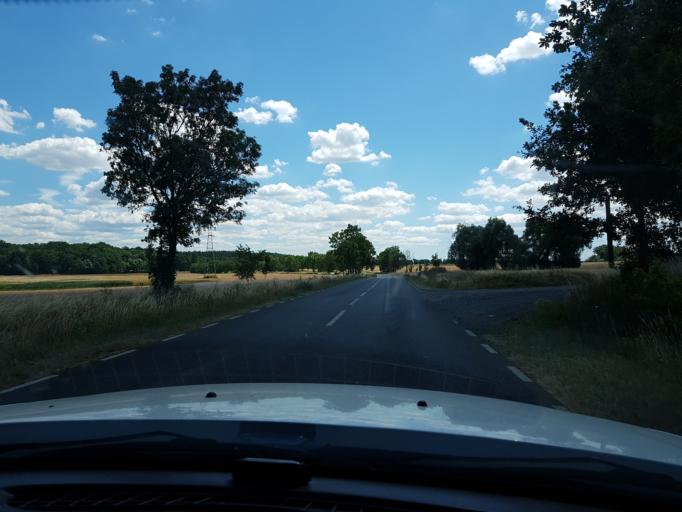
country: PL
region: West Pomeranian Voivodeship
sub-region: Powiat mysliborski
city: Mysliborz
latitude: 52.9166
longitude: 14.9075
